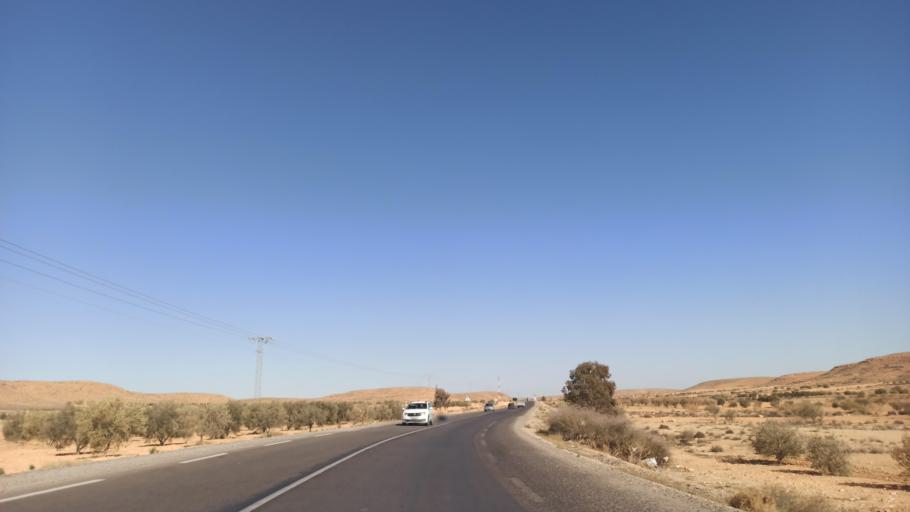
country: TN
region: Sidi Bu Zayd
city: Bi'r al Hufayy
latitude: 34.7079
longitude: 9.0471
